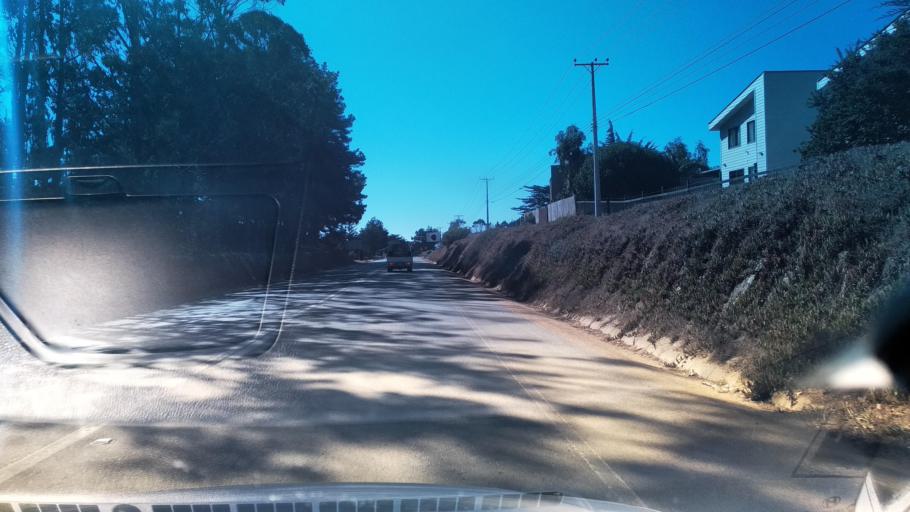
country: CL
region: O'Higgins
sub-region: Provincia de Colchagua
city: Santa Cruz
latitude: -34.4241
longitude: -72.0309
